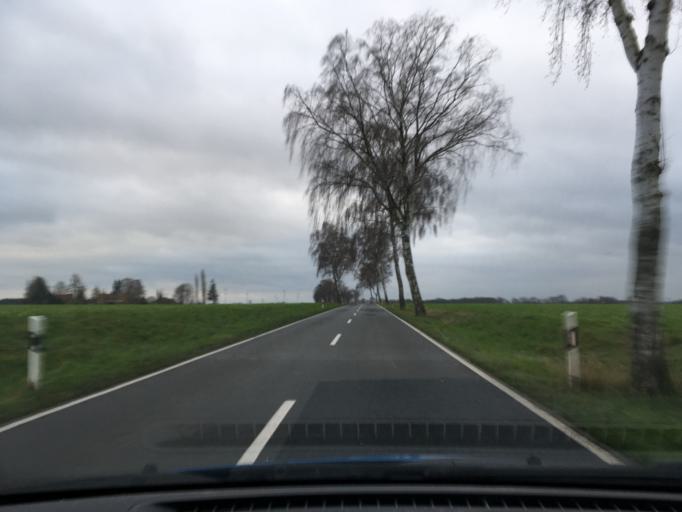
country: DE
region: Lower Saxony
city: Ebstorf
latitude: 53.0147
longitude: 10.4198
